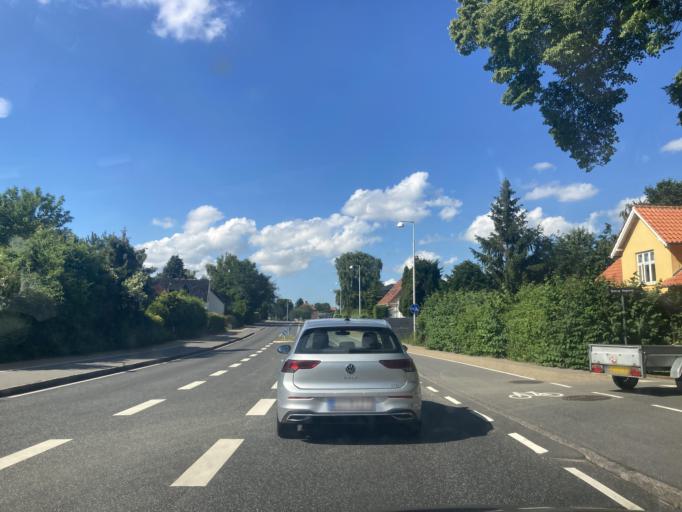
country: DK
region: Capital Region
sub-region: Rudersdal Kommune
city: Birkerod
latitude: 55.8339
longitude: 12.4304
